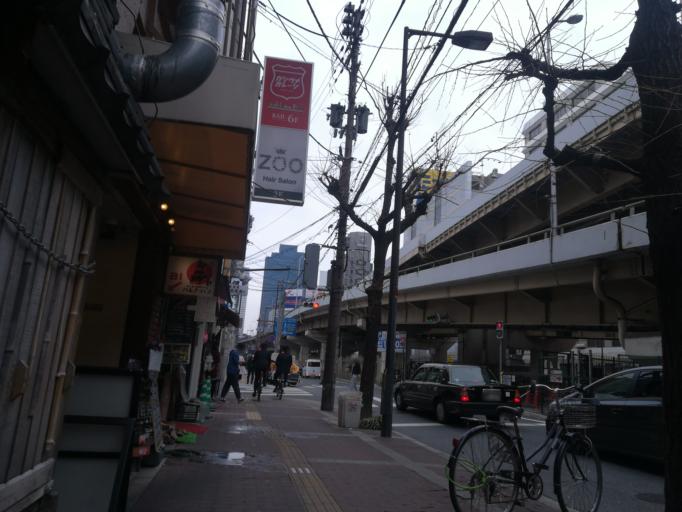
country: JP
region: Osaka
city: Osaka-shi
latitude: 34.7006
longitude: 135.5019
